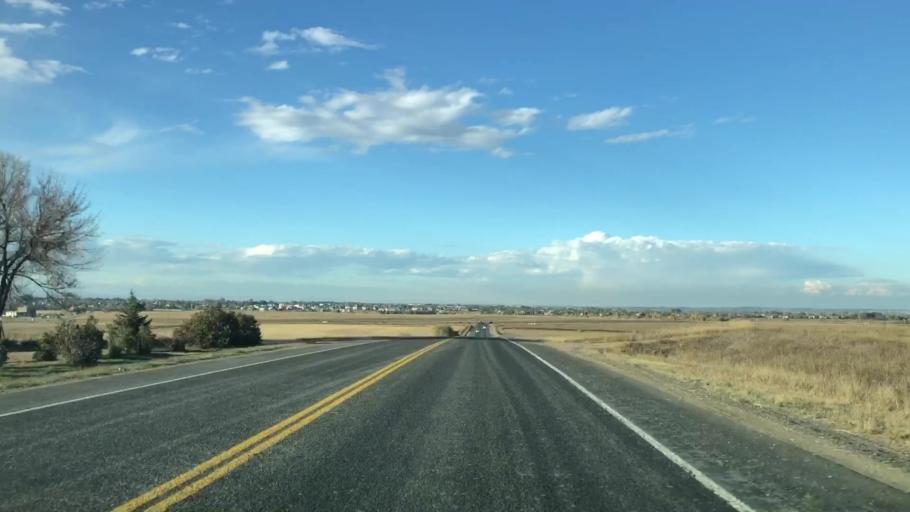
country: US
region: Colorado
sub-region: Larimer County
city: Loveland
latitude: 40.4732
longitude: -105.0202
